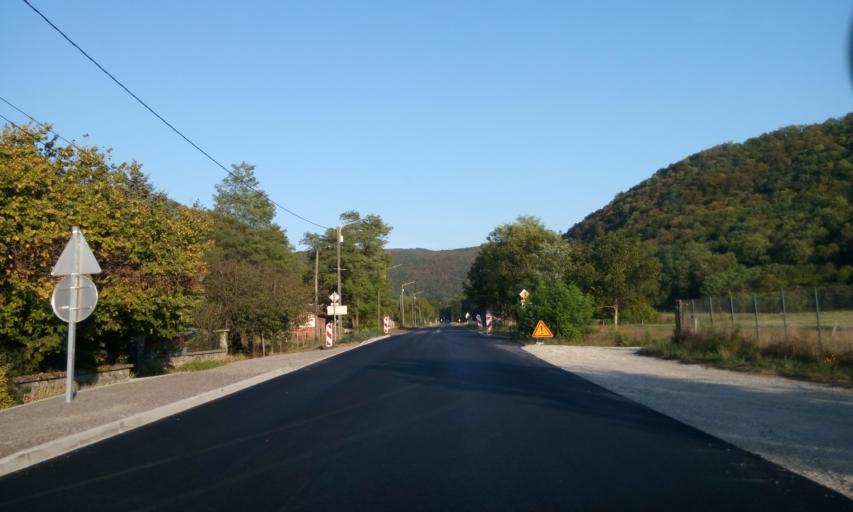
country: FR
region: Rhone-Alpes
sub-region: Departement de l'Ain
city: Poncin
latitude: 46.0778
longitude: 5.4285
